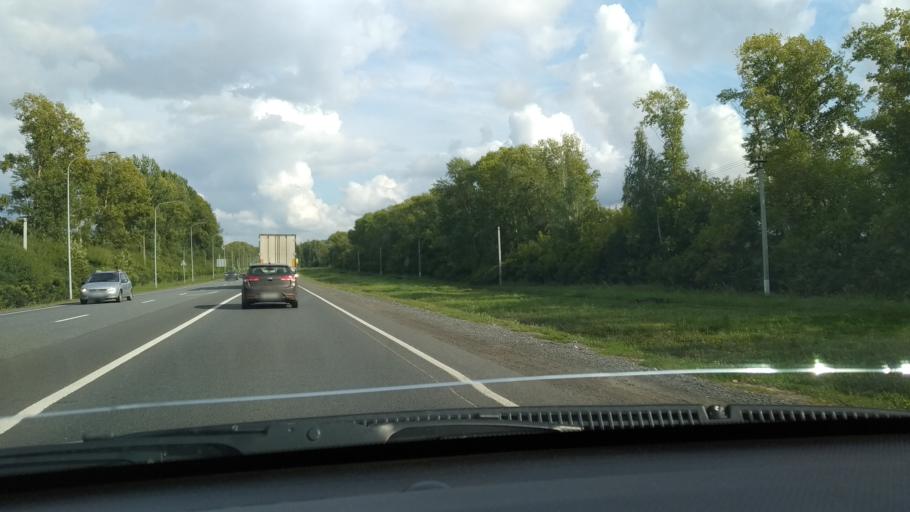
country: RU
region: Tatarstan
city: Stolbishchi
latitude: 55.6547
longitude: 49.3147
